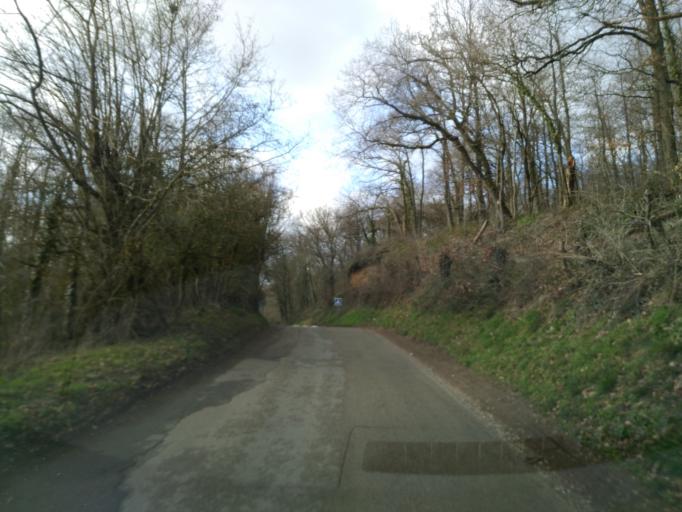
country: FR
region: Ile-de-France
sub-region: Departement des Yvelines
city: Saint-Nom-la-Breteche
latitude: 48.8725
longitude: 2.0057
